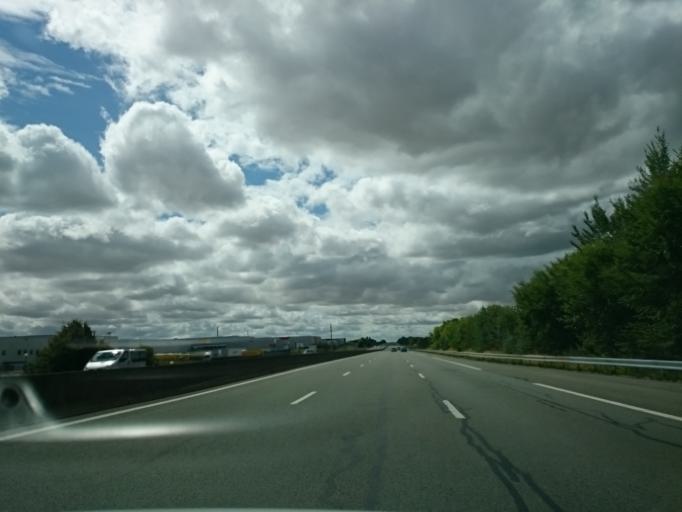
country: FR
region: Centre
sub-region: Departement d'Eure-et-Loir
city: Le Coudray
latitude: 48.4378
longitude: 1.5239
